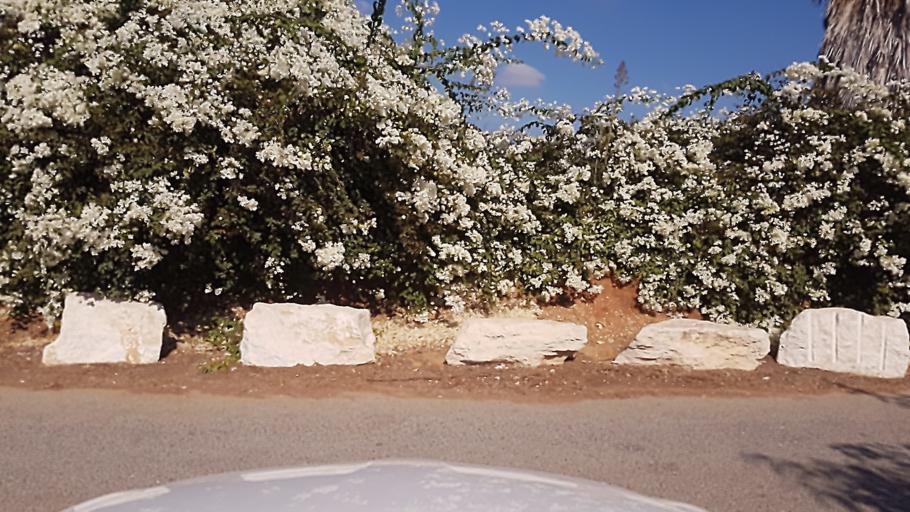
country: IL
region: Central District
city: Kfar Saba
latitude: 32.2105
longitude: 34.9058
